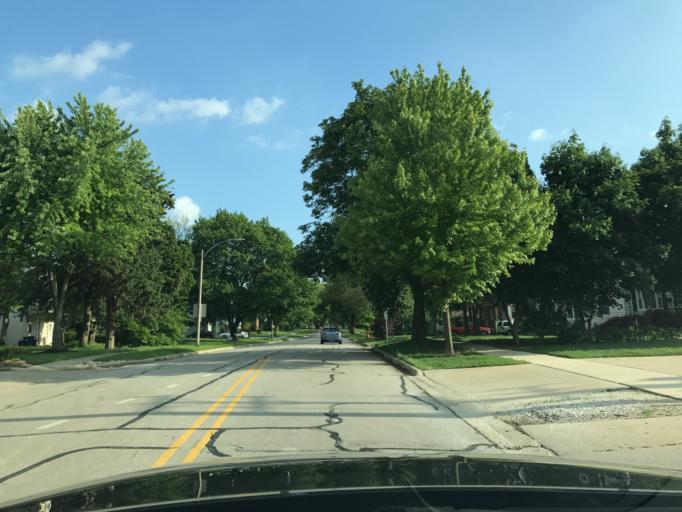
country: US
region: Illinois
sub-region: DuPage County
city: Naperville
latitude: 41.7855
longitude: -88.1413
